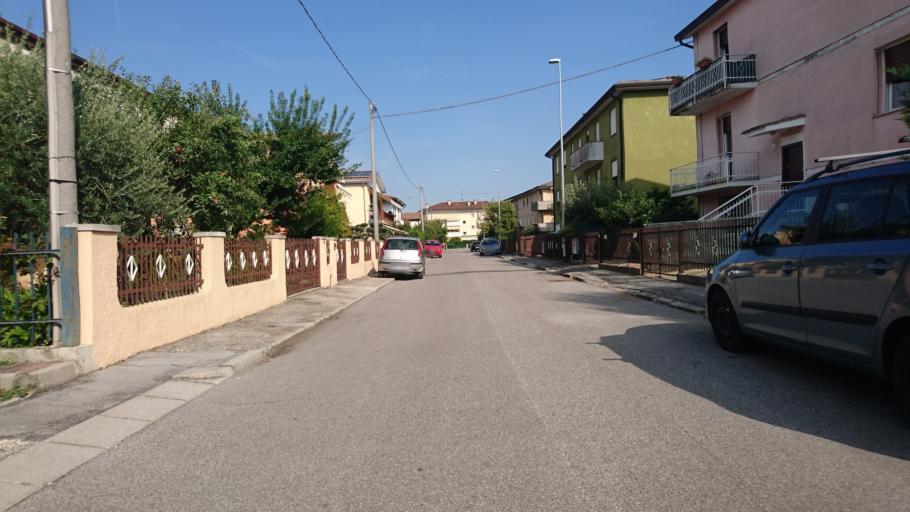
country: IT
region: Veneto
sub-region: Provincia di Padova
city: Tencarola
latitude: 45.3945
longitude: 11.8043
